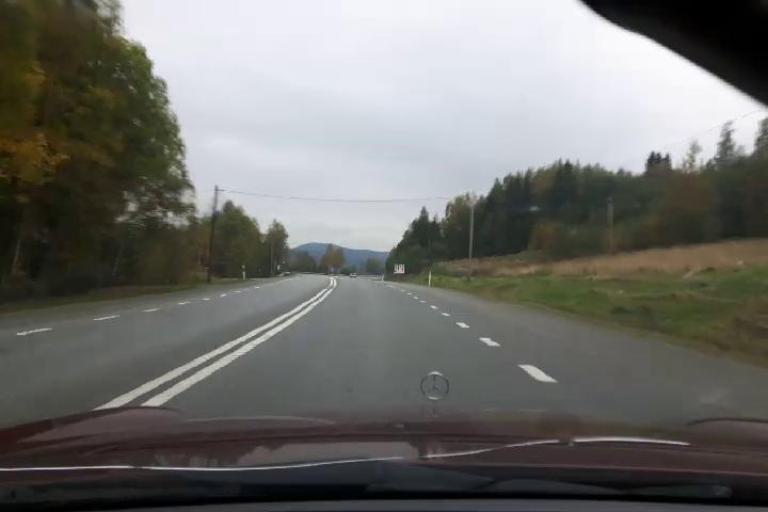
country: SE
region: Vaesternorrland
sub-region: Kramfors Kommun
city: Nordingra
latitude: 63.0084
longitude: 18.2885
